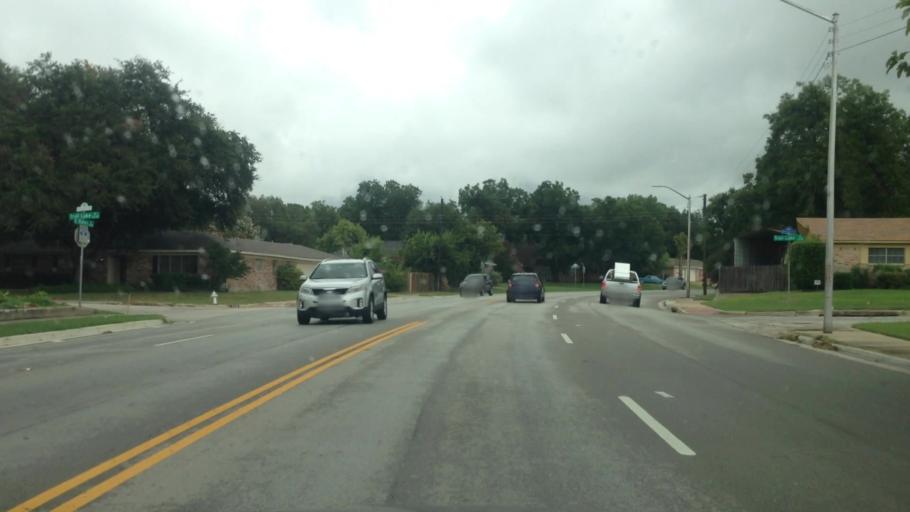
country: US
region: Texas
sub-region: Tarrant County
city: Edgecliff Village
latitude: 32.6583
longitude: -97.3970
